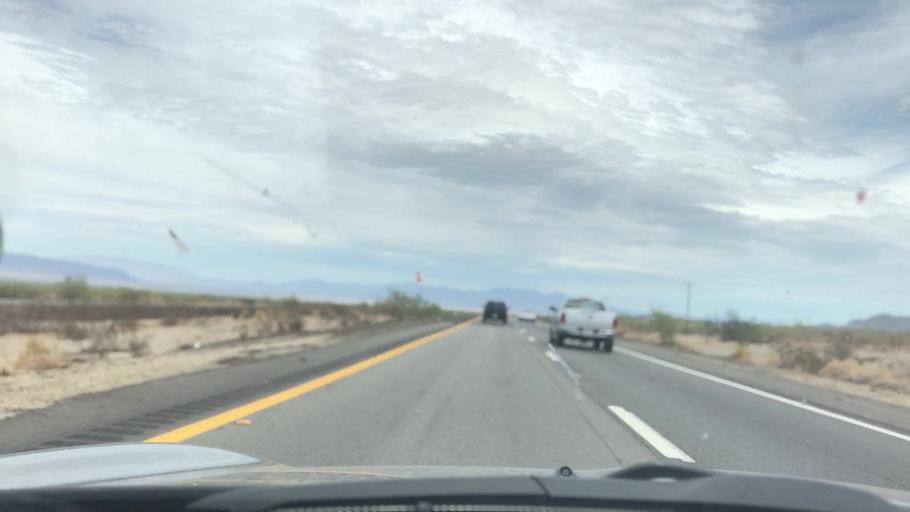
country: US
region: California
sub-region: Imperial County
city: Niland
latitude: 33.6974
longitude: -115.4748
